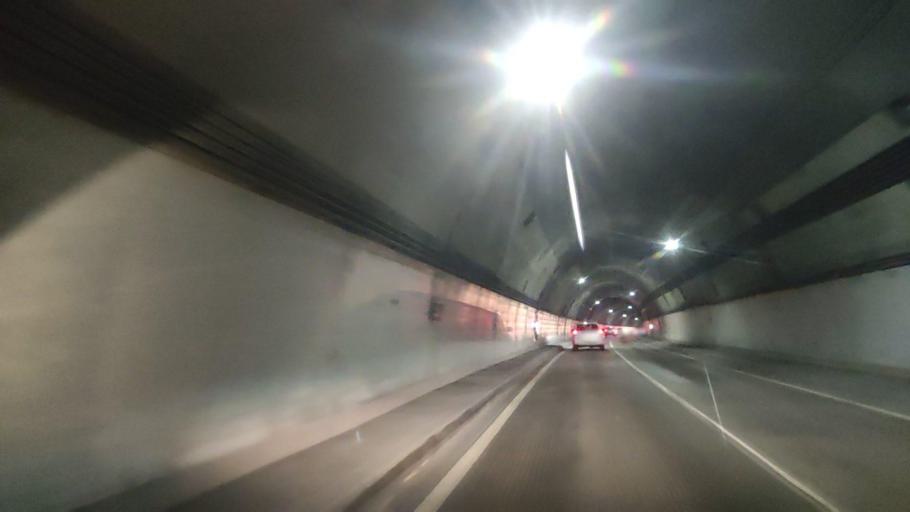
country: JP
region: Hokkaido
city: Ishikari
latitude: 43.4441
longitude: 141.4130
